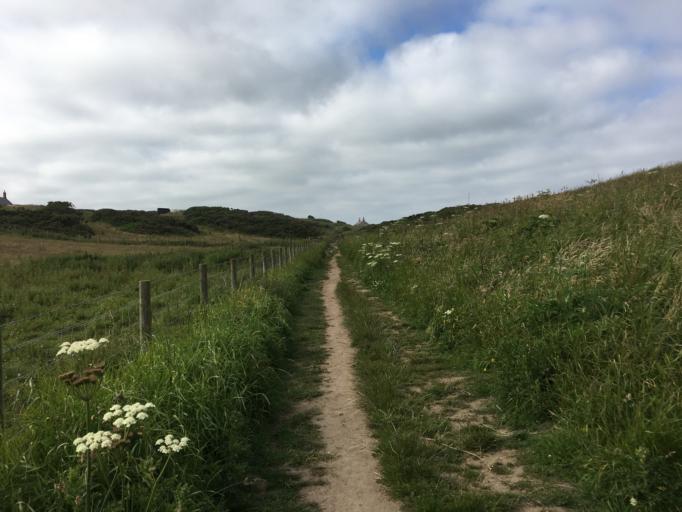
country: GB
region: England
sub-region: Northumberland
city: Alnmouth
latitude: 55.4473
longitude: -1.5880
